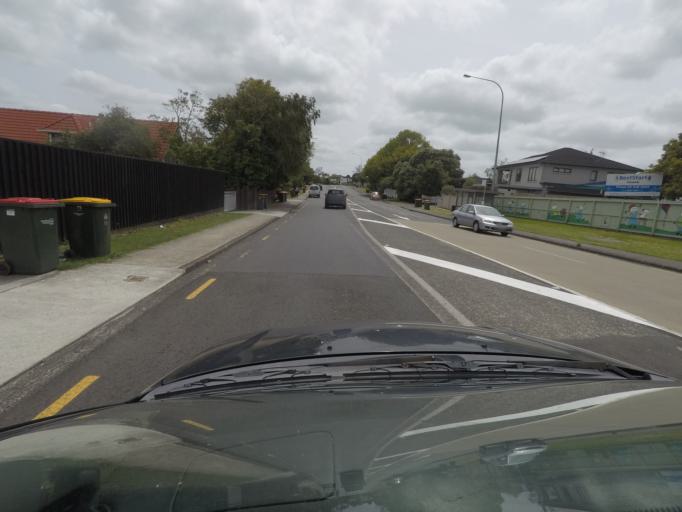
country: NZ
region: Auckland
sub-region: Auckland
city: Pakuranga
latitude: -36.8981
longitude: 174.9202
